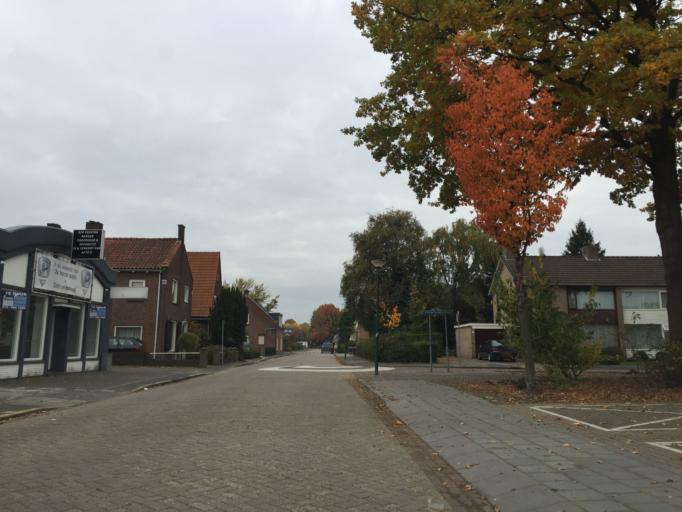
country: NL
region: North Brabant
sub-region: Gemeente Waalwijk
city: Waalwijk
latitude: 51.6585
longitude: 5.0300
